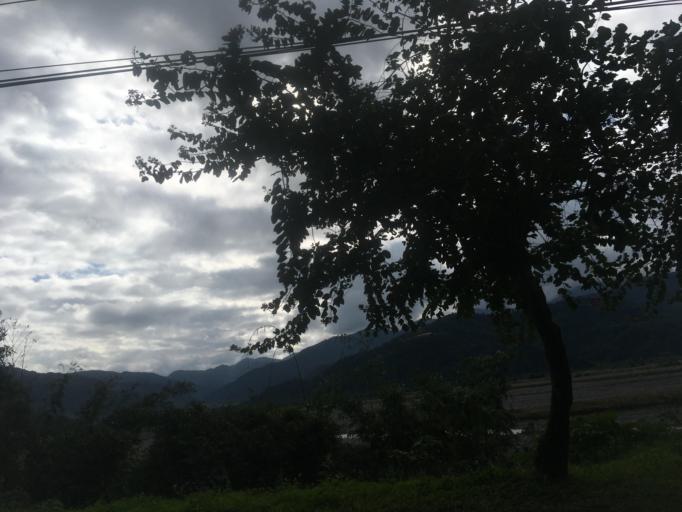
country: TW
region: Taiwan
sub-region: Yilan
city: Yilan
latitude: 24.6559
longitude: 121.5842
